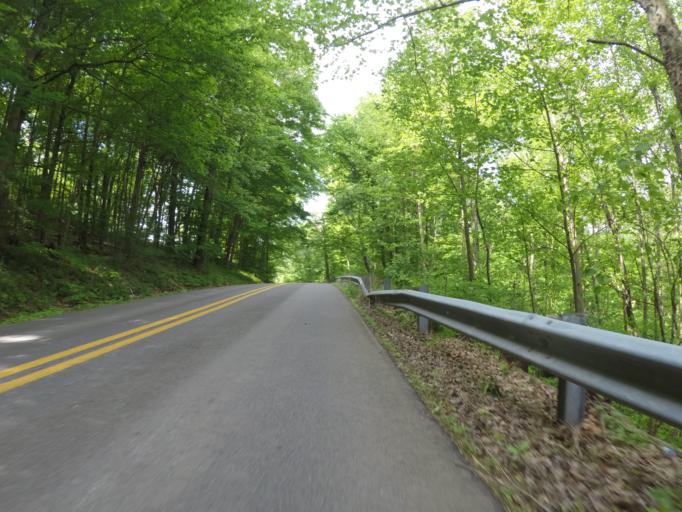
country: US
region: West Virginia
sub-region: Wayne County
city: Ceredo
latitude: 38.3407
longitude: -82.5741
